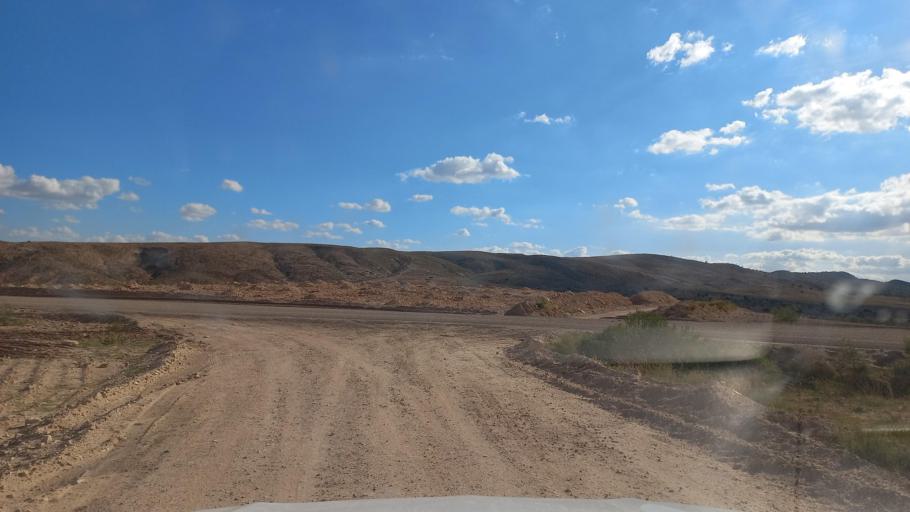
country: TN
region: Al Qasrayn
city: Sbiba
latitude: 35.3952
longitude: 9.0144
